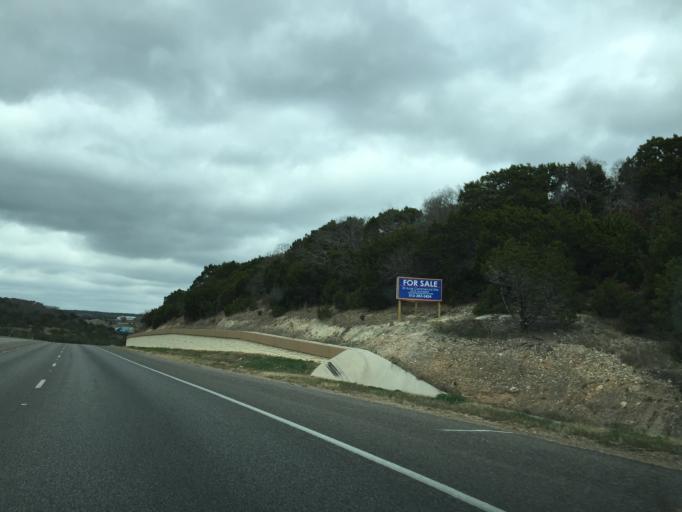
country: US
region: Texas
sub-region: Travis County
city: The Hills
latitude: 30.3351
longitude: -98.0302
